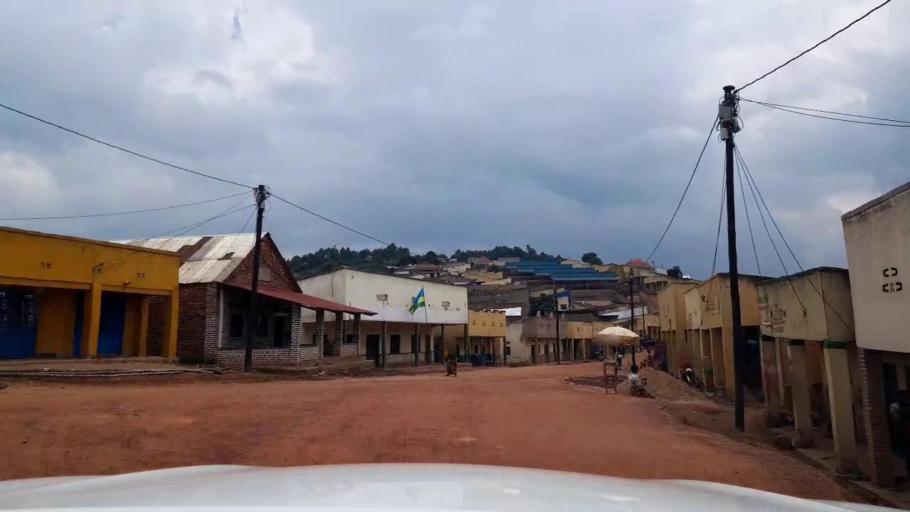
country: RW
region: Northern Province
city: Byumba
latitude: -1.5001
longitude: 29.9349
